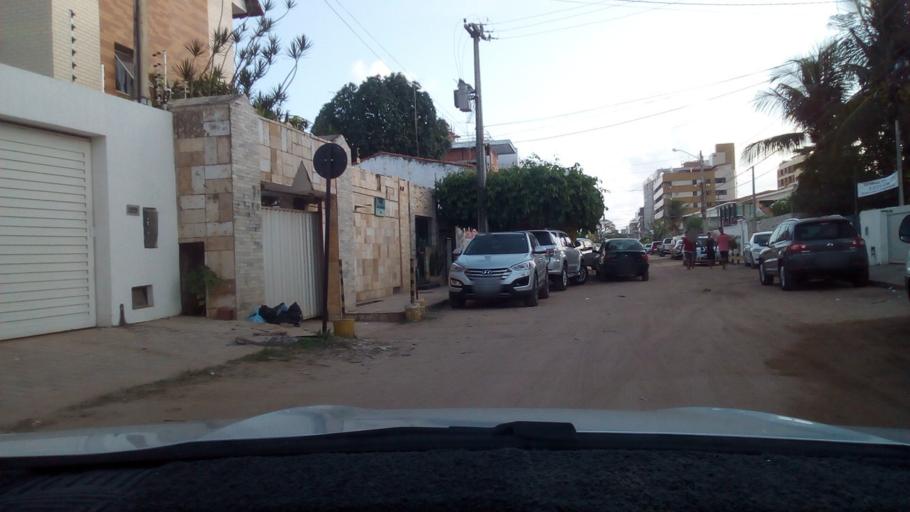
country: BR
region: Paraiba
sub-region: Cabedelo
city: Cabedelo
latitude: -7.0065
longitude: -34.8269
